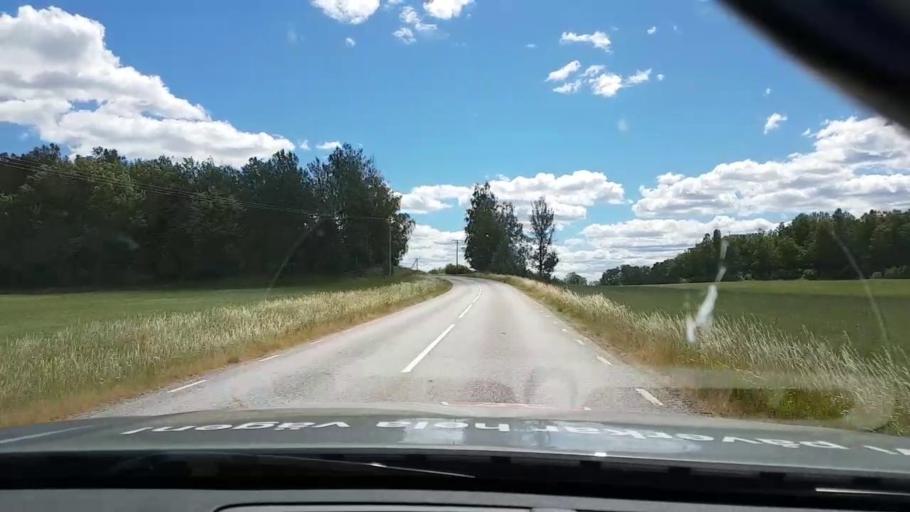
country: SE
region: Kalmar
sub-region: Vasterviks Kommun
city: Overum
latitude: 58.0520
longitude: 16.4059
